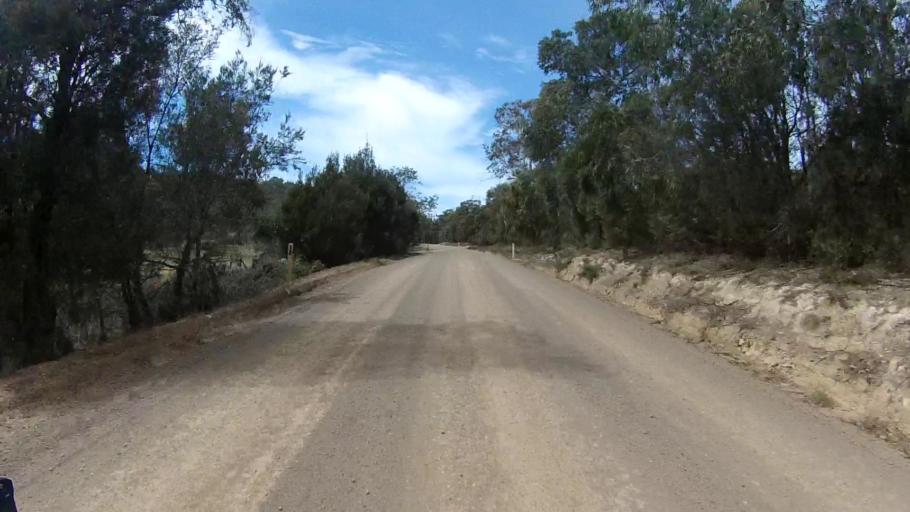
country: AU
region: Tasmania
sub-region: Sorell
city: Sorell
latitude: -42.8002
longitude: 147.6639
